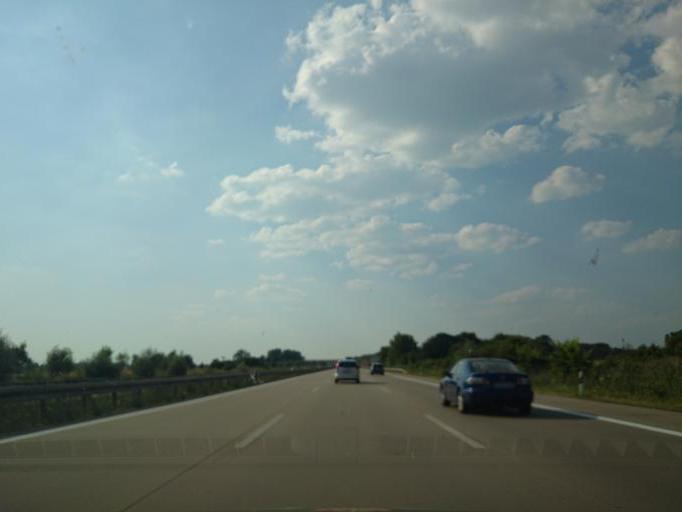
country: DE
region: Brandenburg
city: Ahrensfelde
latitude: 52.5903
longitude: 13.6225
